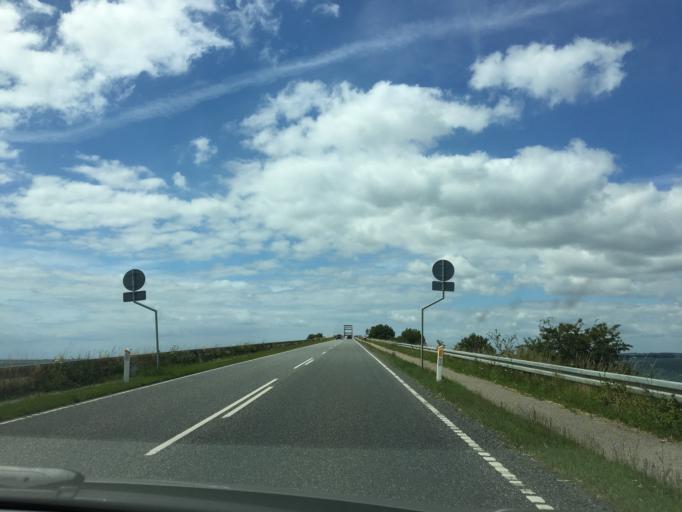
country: DK
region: South Denmark
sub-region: Langeland Kommune
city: Rudkobing
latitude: 54.9451
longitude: 10.7175
